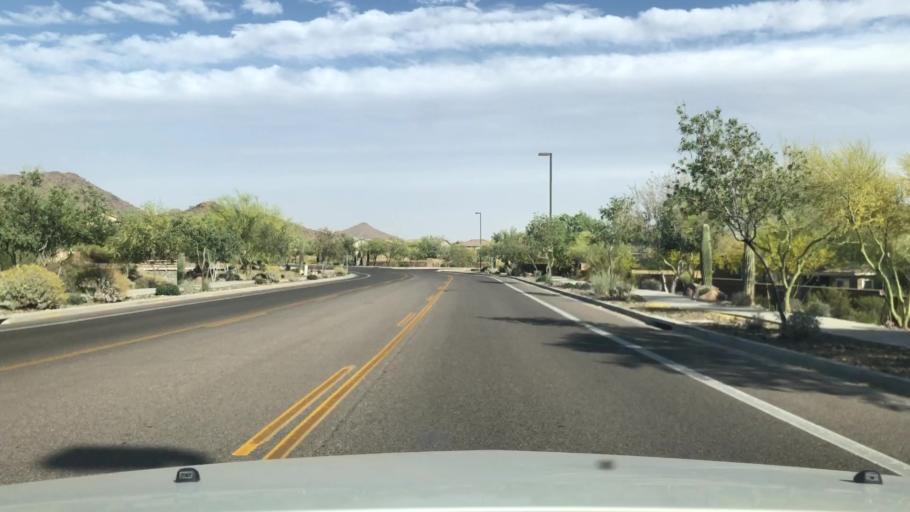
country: US
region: Arizona
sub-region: Maricopa County
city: Anthem
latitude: 33.7311
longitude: -112.0980
